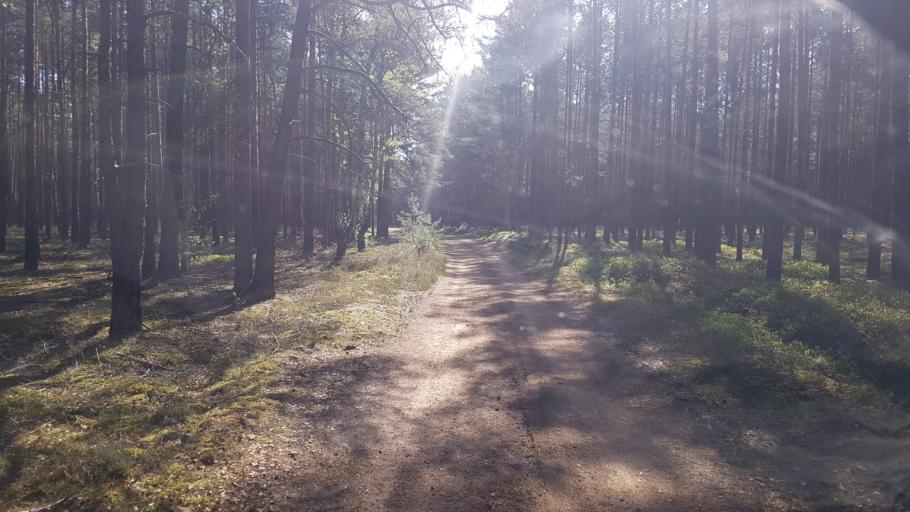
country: DE
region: Brandenburg
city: Crinitz
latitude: 51.7358
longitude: 13.7811
